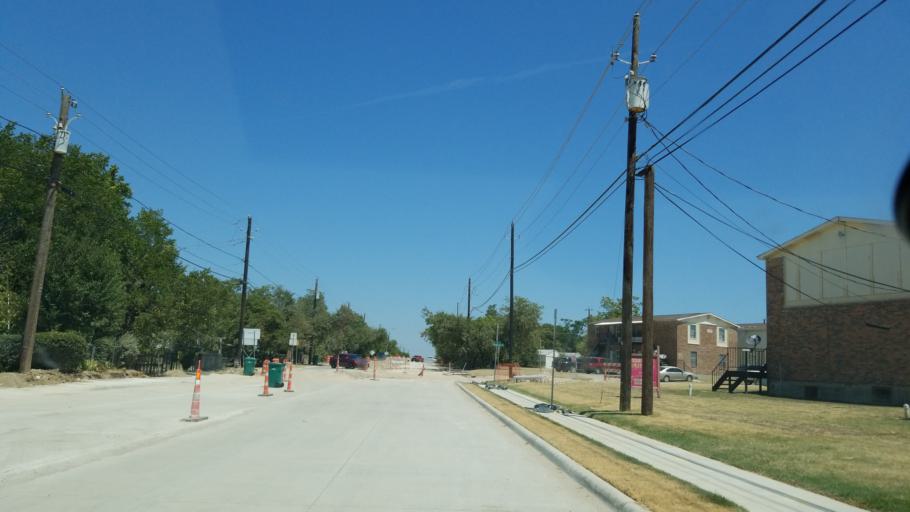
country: US
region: Texas
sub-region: Dallas County
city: Cockrell Hill
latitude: 32.7444
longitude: -96.8913
